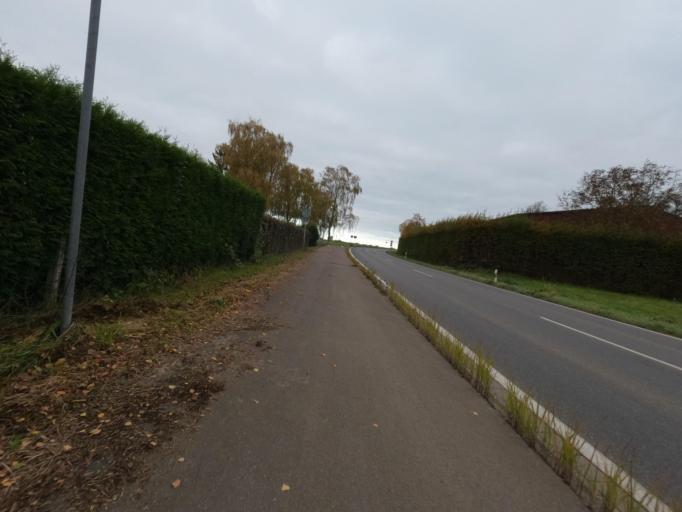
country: DE
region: North Rhine-Westphalia
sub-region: Regierungsbezirk Koln
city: Linnich
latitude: 50.9666
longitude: 6.3178
